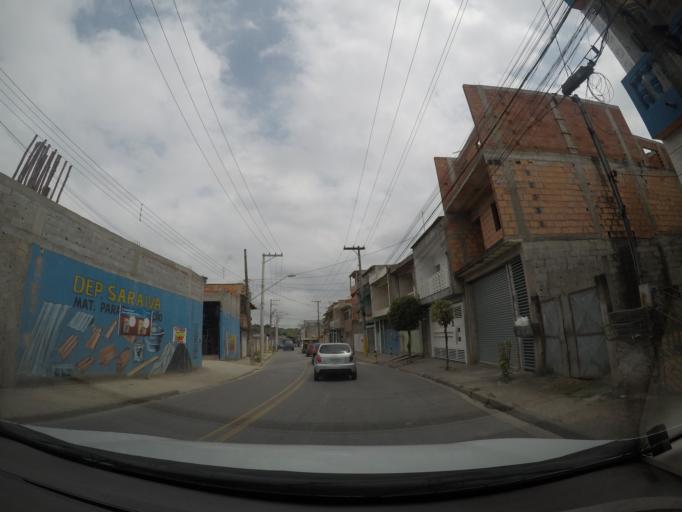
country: BR
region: Sao Paulo
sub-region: Itaquaquecetuba
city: Itaquaquecetuba
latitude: -23.4416
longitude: -46.3791
